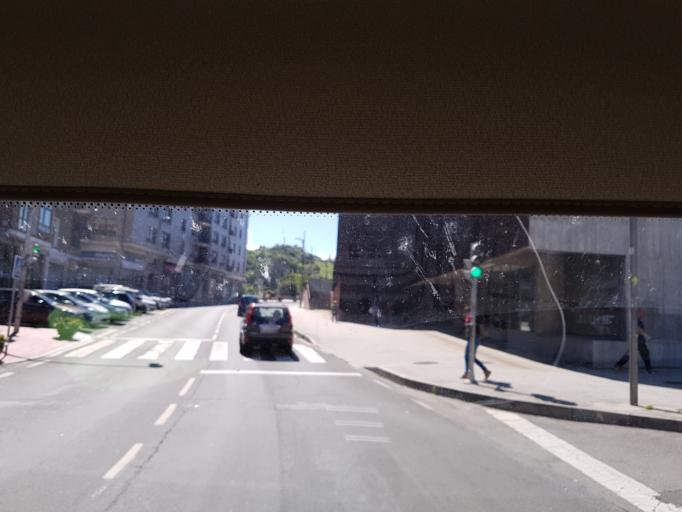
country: ES
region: Basque Country
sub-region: Bizkaia
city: Urtuella
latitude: 43.3093
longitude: -3.0537
